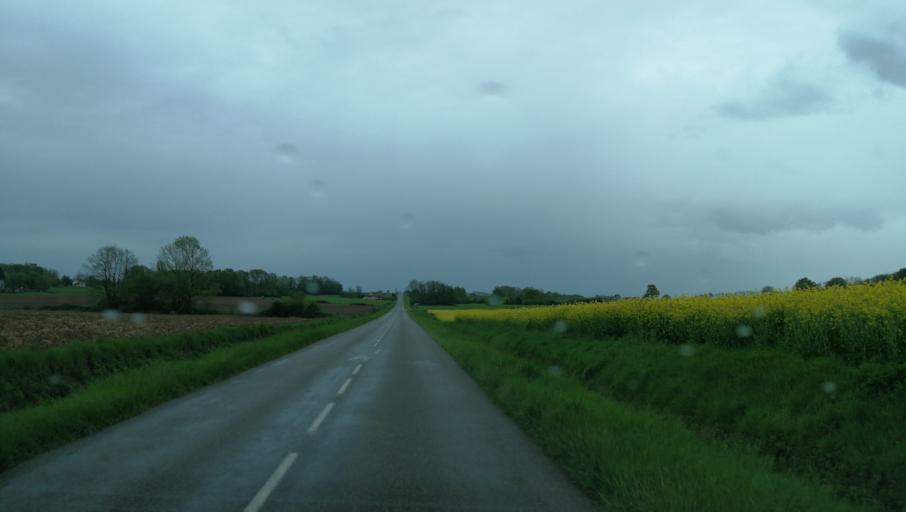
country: FR
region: Franche-Comte
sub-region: Departement du Jura
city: Bletterans
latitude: 46.8265
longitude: 5.3801
